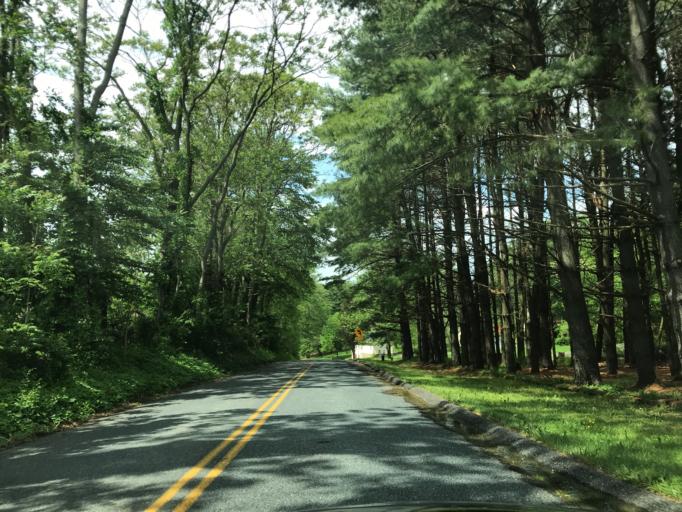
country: US
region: Maryland
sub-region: Harford County
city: Bel Air North
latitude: 39.5984
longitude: -76.3443
